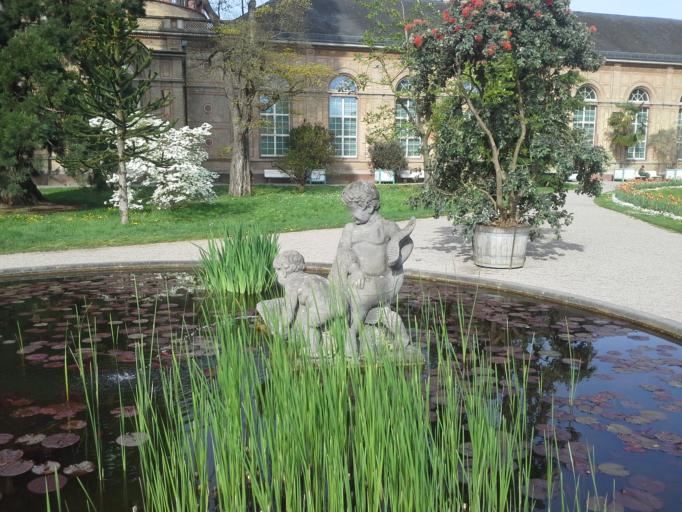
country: DE
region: Baden-Wuerttemberg
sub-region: Karlsruhe Region
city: Karlsruhe
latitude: 49.0130
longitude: 8.3998
